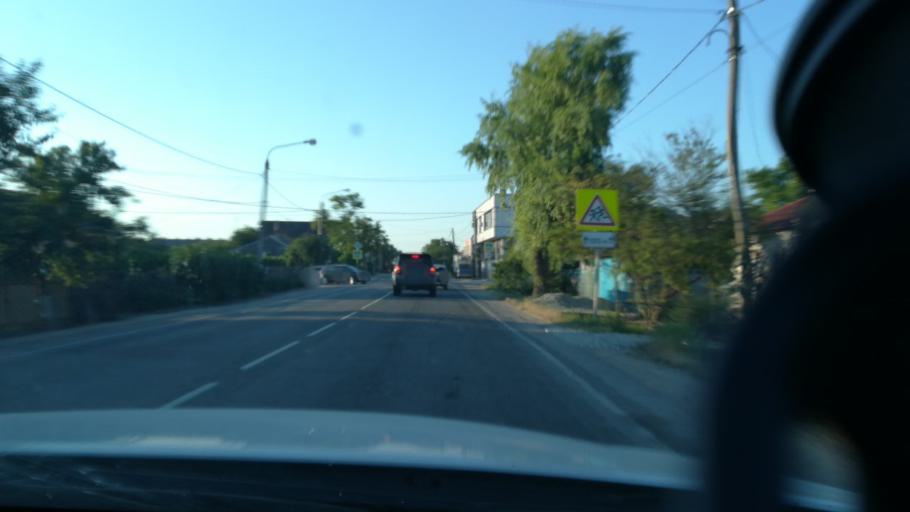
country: RU
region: Krasnodarskiy
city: Gostagayevskaya
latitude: 45.0207
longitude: 37.5027
